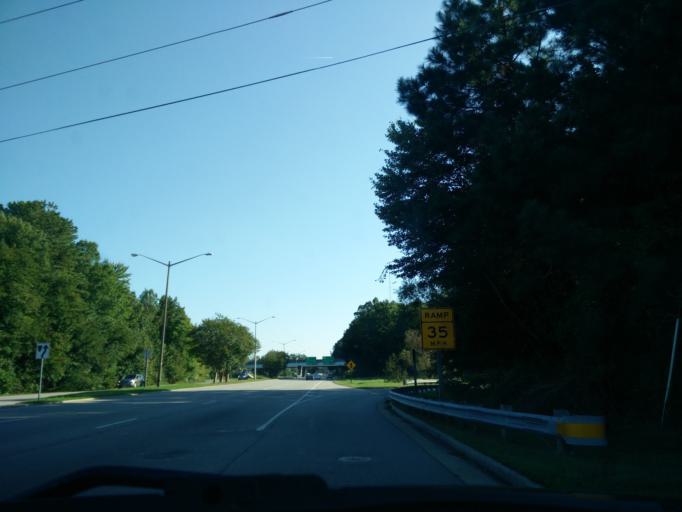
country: US
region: Virginia
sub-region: City of Chesapeake
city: Chesapeake
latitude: 36.7393
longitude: -76.2424
